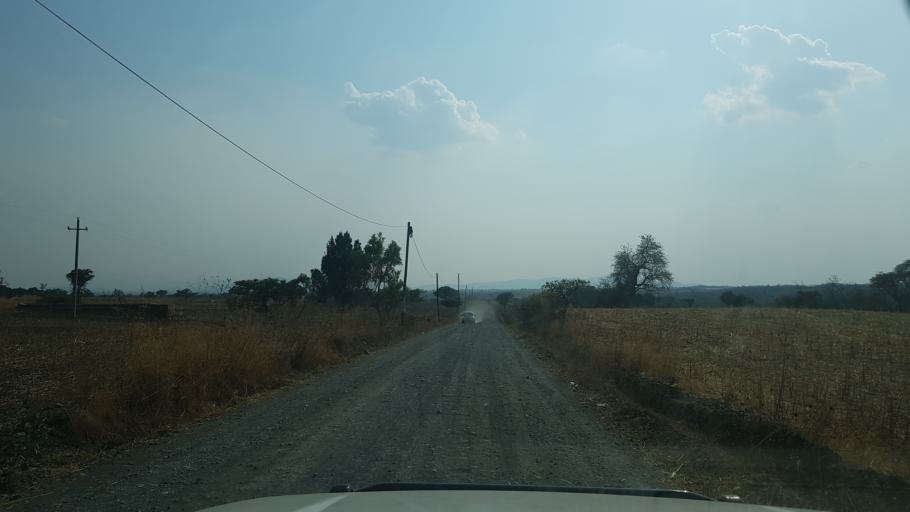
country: MX
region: Morelos
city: Tlacotepec
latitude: 18.7776
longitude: -98.7290
